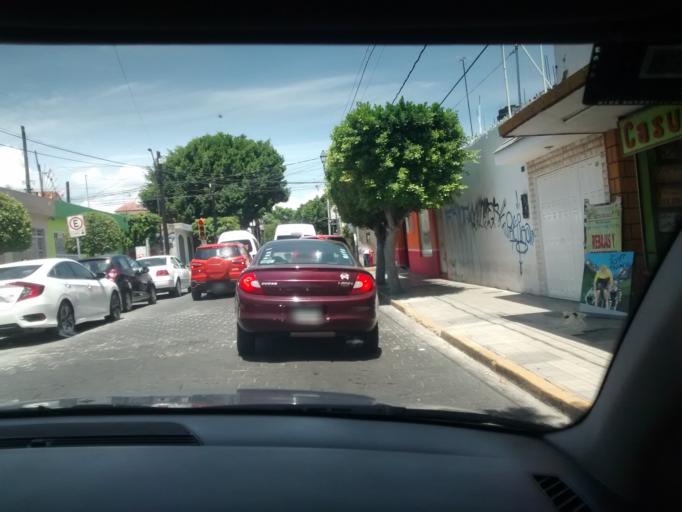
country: MX
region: Puebla
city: Tehuacan
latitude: 18.4610
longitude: -97.3963
